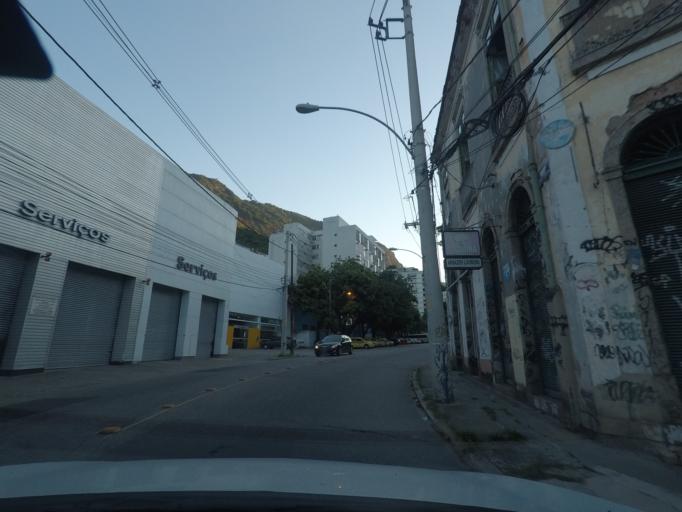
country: BR
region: Rio de Janeiro
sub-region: Rio De Janeiro
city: Rio de Janeiro
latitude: -22.9450
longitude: -43.2544
